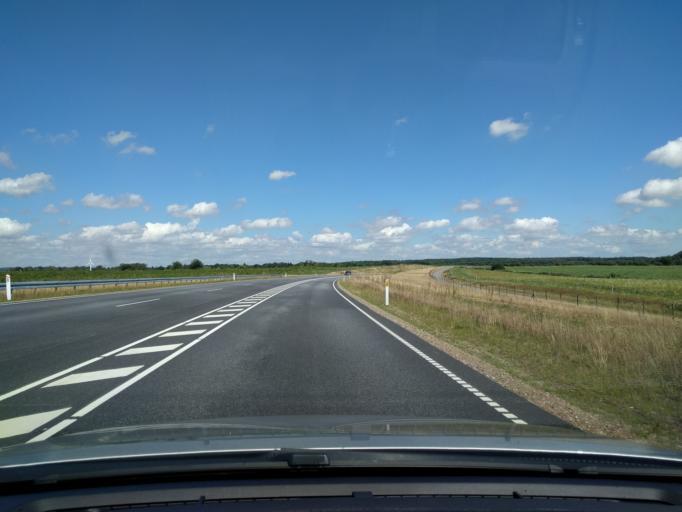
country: DK
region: Zealand
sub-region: Naestved Kommune
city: Naestved
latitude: 55.2578
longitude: 11.7346
